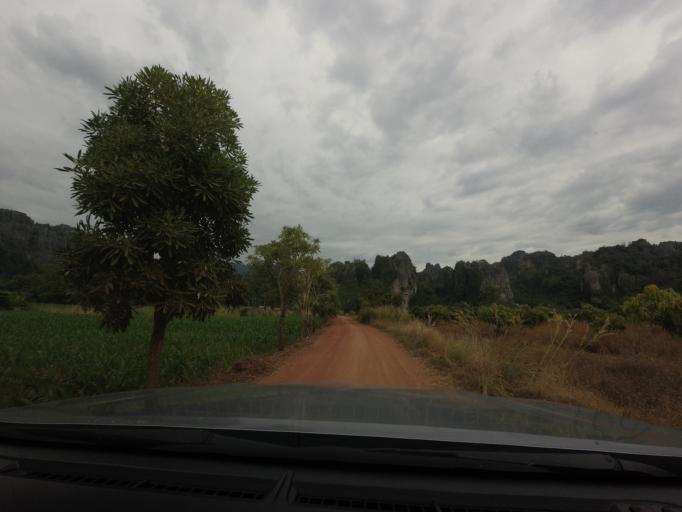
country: TH
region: Phitsanulok
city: Noen Maprang
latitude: 16.5793
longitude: 100.6839
